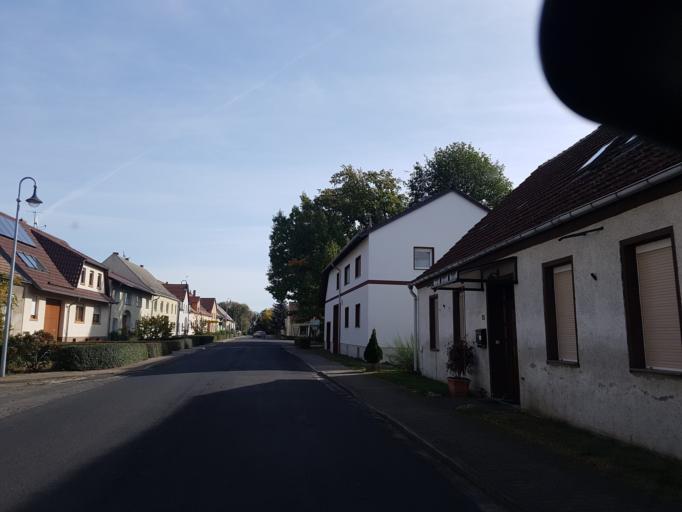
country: DE
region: Brandenburg
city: Schlieben
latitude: 51.7030
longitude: 13.4136
